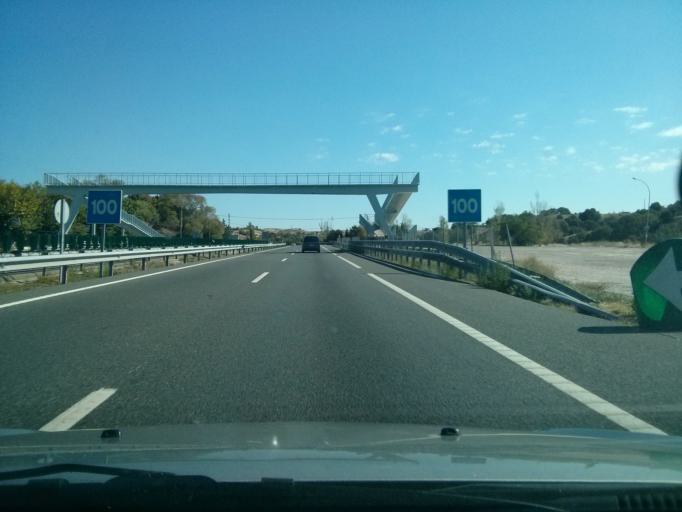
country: ES
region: Madrid
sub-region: Provincia de Madrid
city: San Agustin de Guadalix
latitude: 40.6925
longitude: -3.5942
